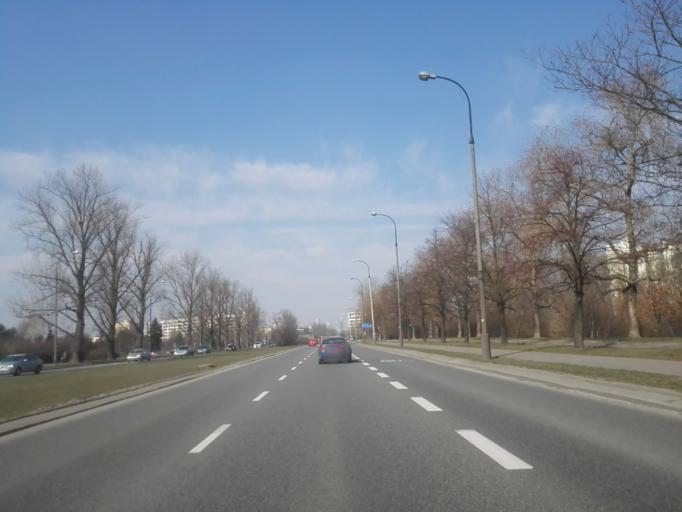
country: PL
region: Masovian Voivodeship
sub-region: Warszawa
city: Mokotow
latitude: 52.1933
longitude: 21.0440
